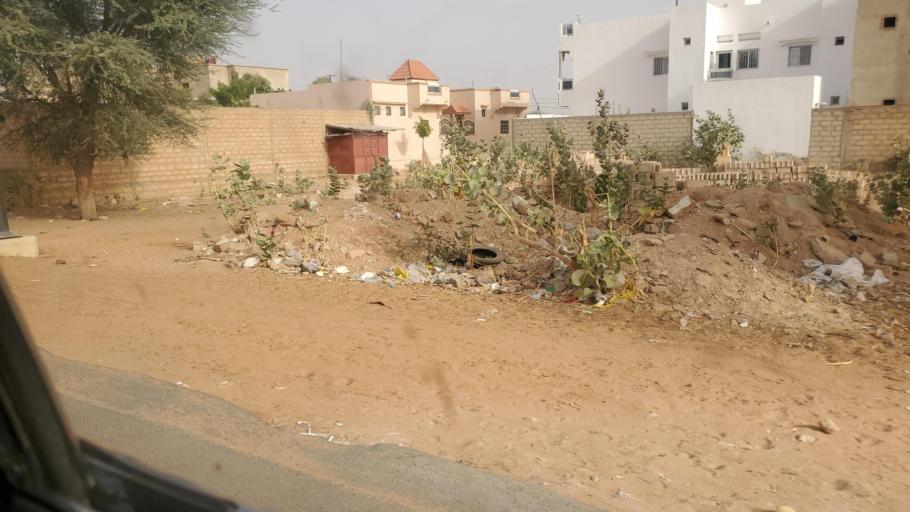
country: SN
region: Louga
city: Louga
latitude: 15.6266
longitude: -16.2410
